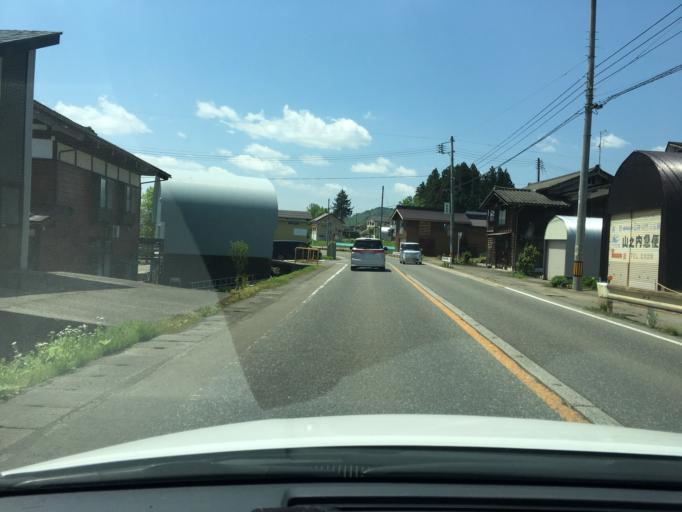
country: JP
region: Niigata
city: Ojiya
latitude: 37.2715
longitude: 138.9766
